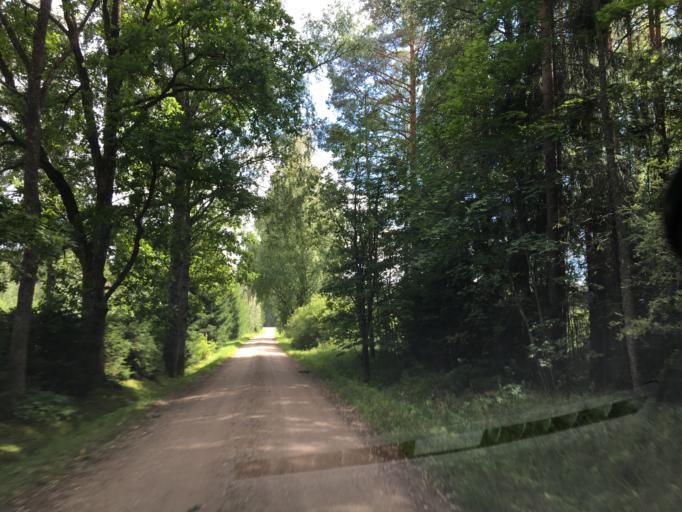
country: EE
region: Paernumaa
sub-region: Vaendra vald (alev)
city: Vandra
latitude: 58.5818
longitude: 25.2493
